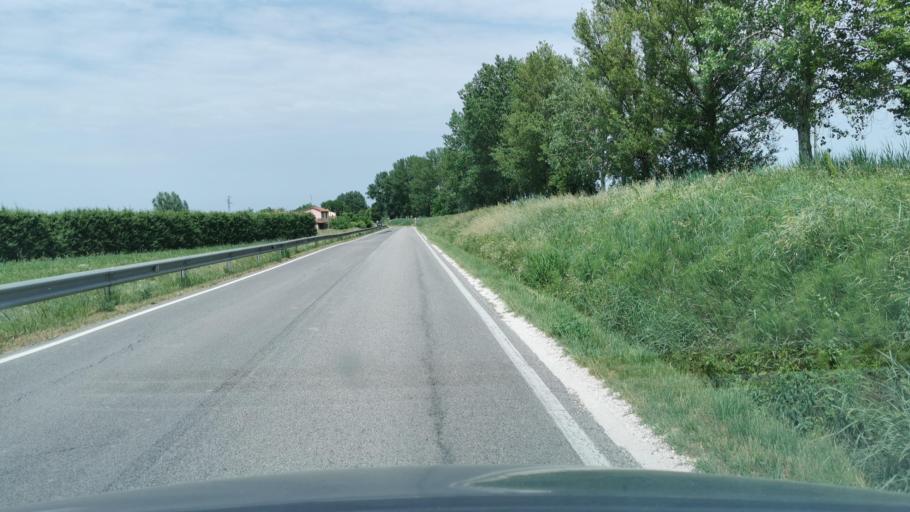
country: IT
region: Emilia-Romagna
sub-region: Provincia di Ravenna
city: Alfonsine
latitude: 44.4871
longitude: 12.0491
